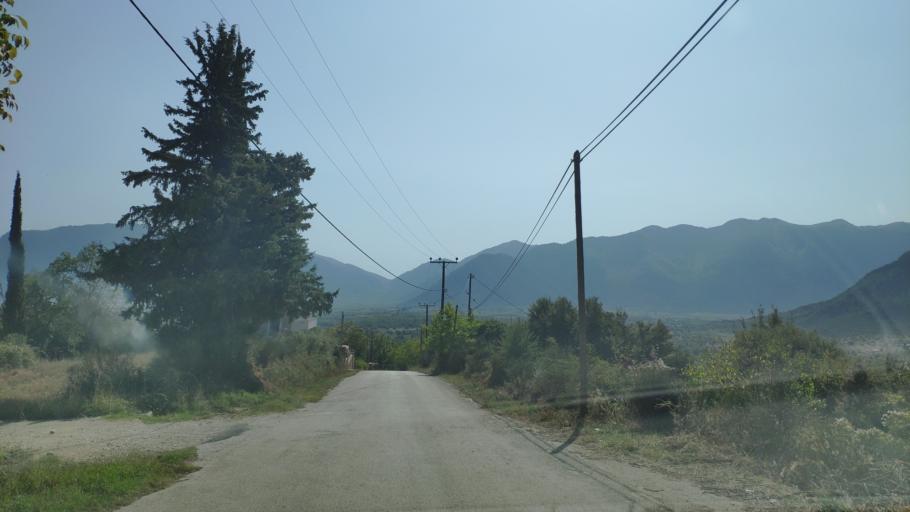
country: GR
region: West Greece
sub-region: Nomos Achaias
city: Kalavryta
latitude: 37.9177
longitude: 22.2991
